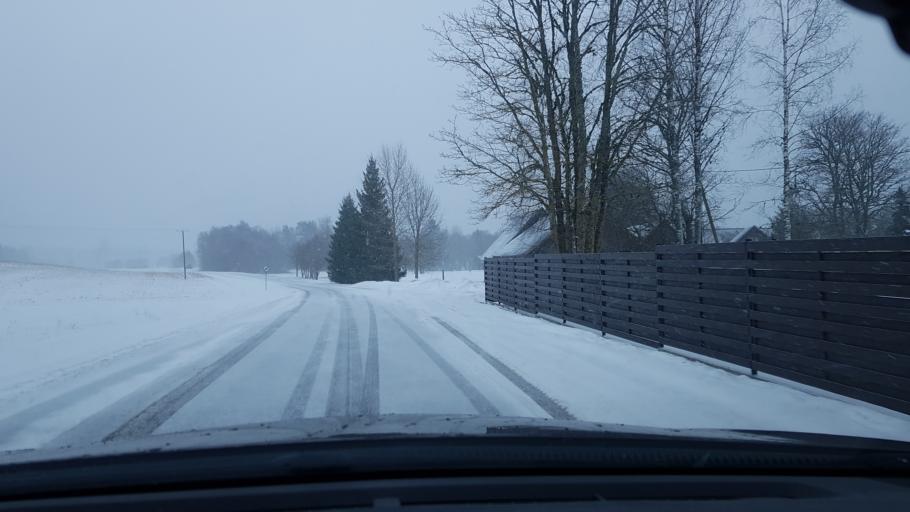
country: EE
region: Harju
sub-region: Anija vald
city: Kehra
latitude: 59.2062
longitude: 25.4254
